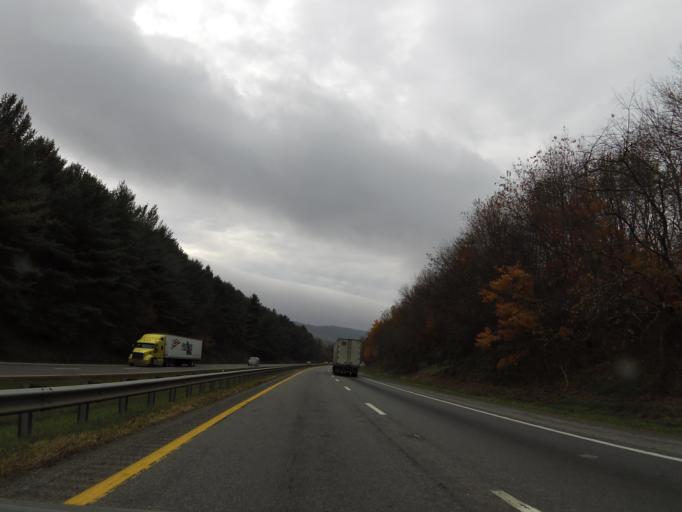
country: US
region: Virginia
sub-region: Bland County
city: Bland
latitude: 37.0653
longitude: -81.1275
